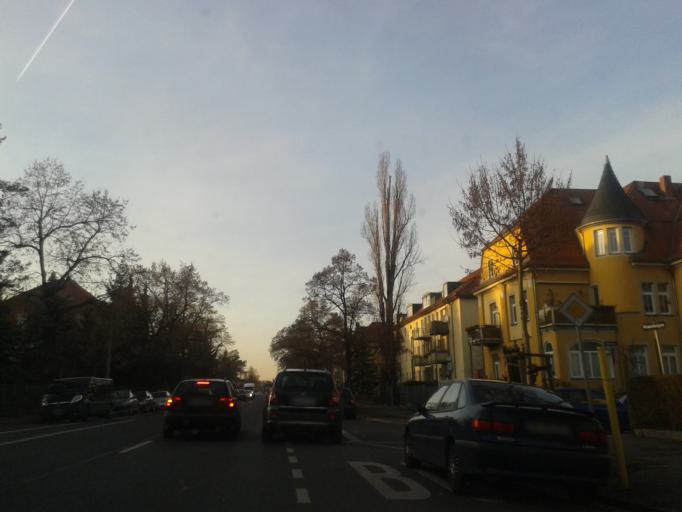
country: DE
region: Saxony
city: Dresden
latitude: 51.0266
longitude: 13.7913
